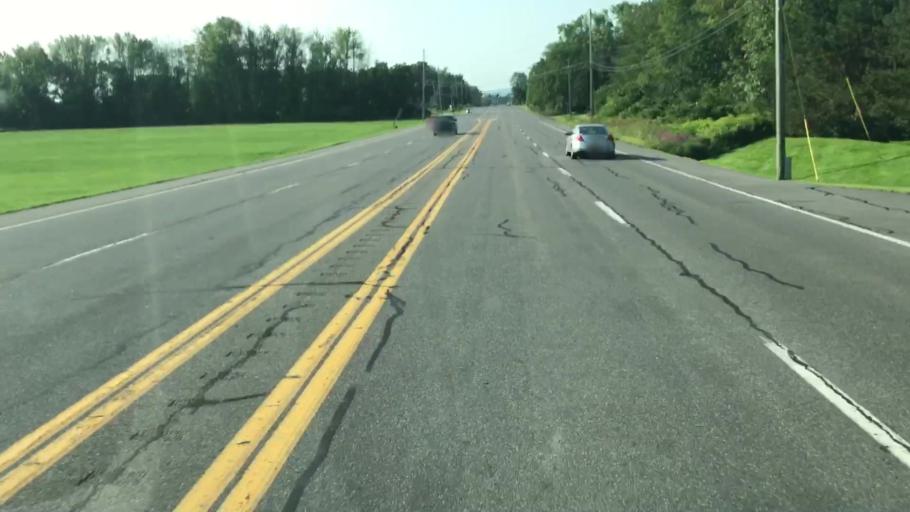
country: US
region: New York
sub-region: Onondaga County
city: Liverpool
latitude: 43.1342
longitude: -76.2062
